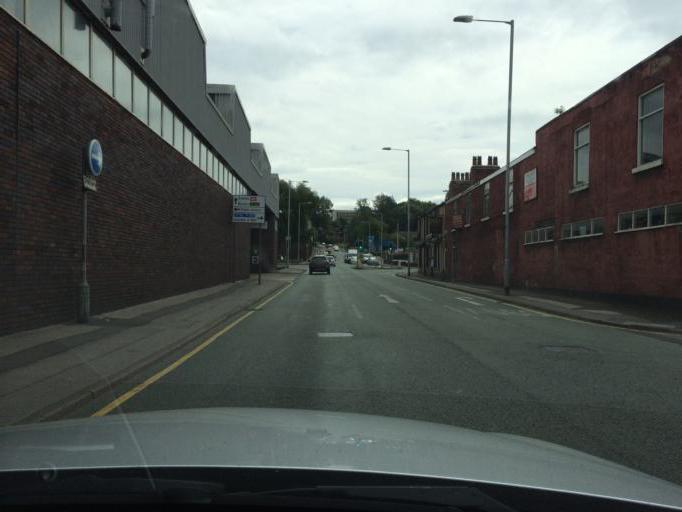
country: GB
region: England
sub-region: Borough of Stockport
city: Stockport
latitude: 53.4081
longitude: -2.1666
